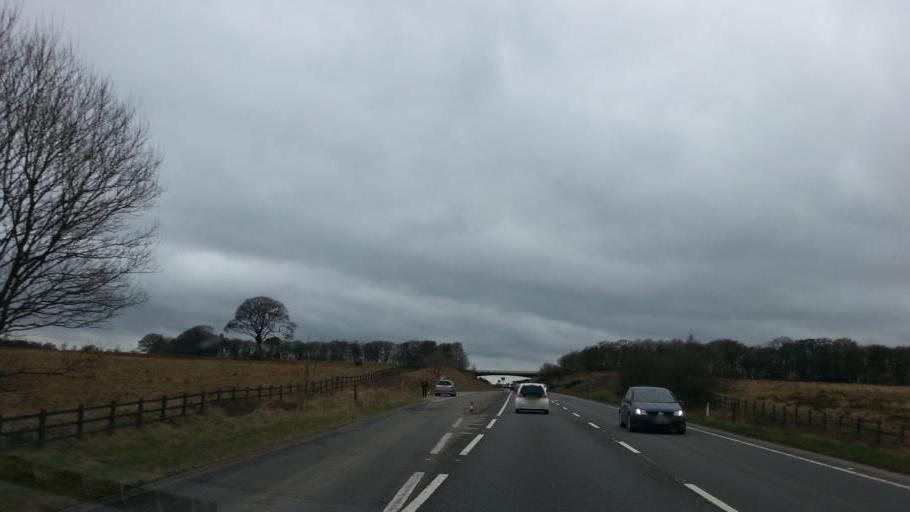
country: GB
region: England
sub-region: Devon
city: Tiverton
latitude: 50.9764
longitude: -3.6329
